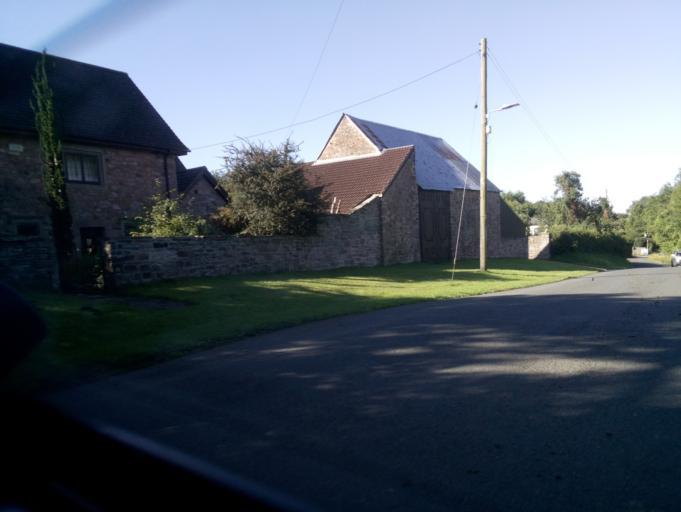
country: GB
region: England
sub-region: Gloucestershire
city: Coleford
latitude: 51.7966
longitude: -2.6351
